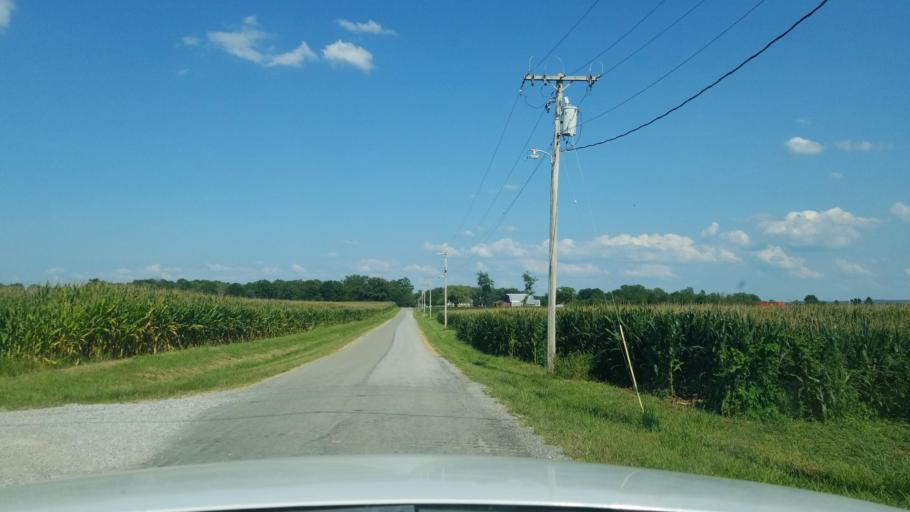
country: US
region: Illinois
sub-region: Saline County
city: Harrisburg
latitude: 37.7865
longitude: -88.4984
